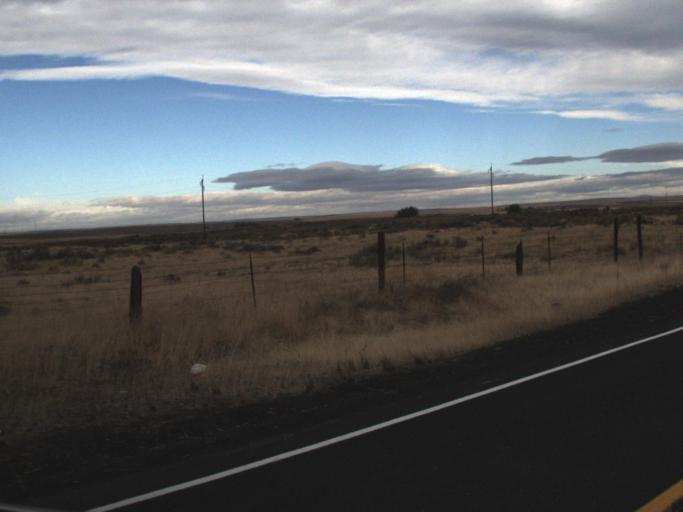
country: US
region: Washington
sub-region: Okanogan County
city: Coulee Dam
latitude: 47.7524
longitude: -118.7217
